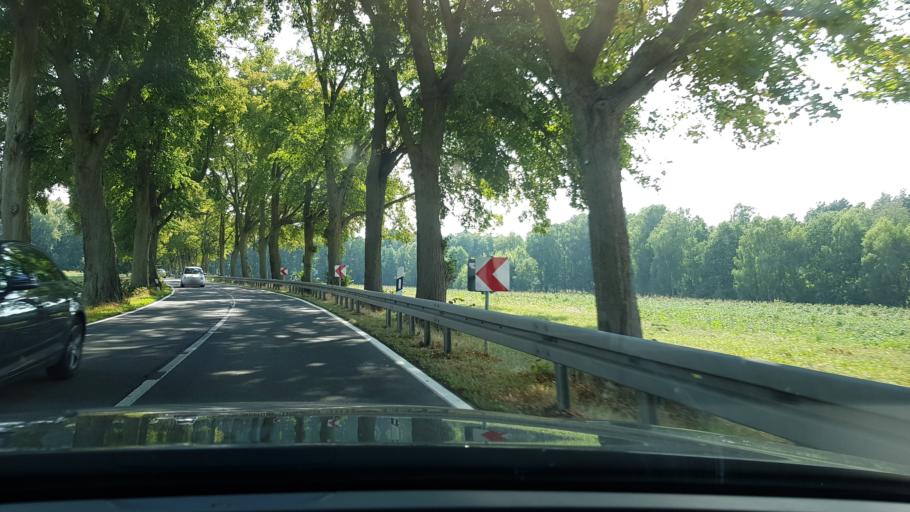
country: DE
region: Brandenburg
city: Lindow
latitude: 53.0131
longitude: 12.9786
